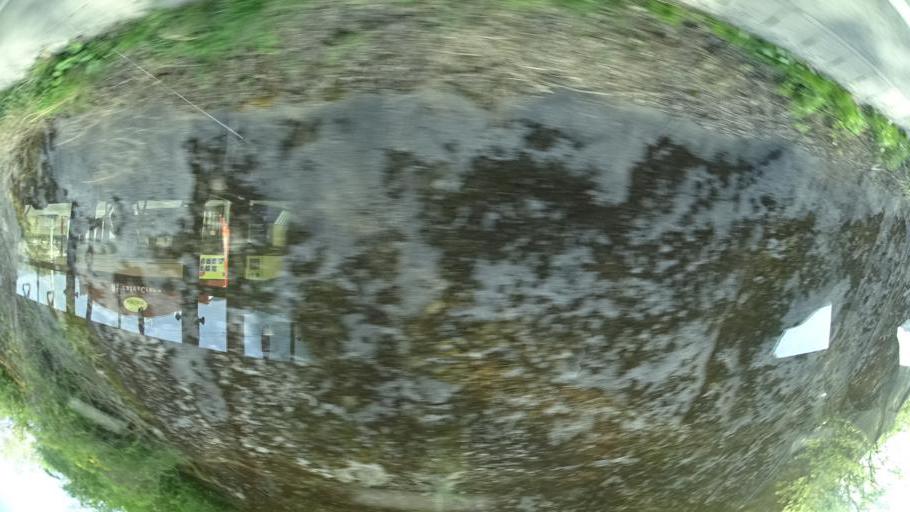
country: JP
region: Iwate
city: Ofunato
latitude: 39.0152
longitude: 141.6656
